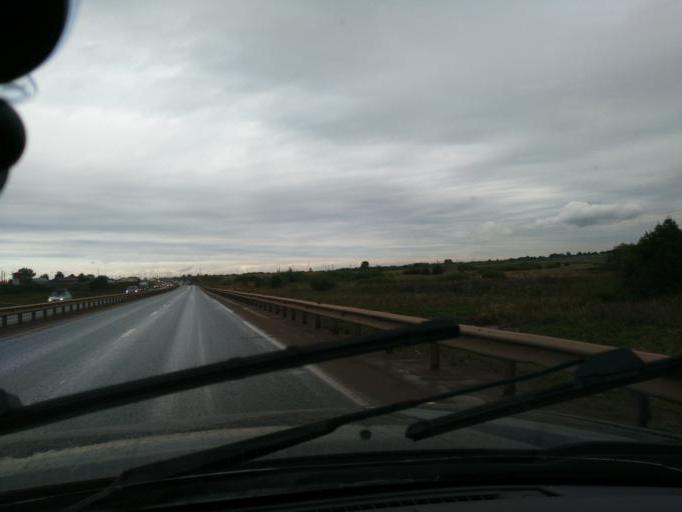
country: RU
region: Perm
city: Kultayevo
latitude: 57.9037
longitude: 55.9813
